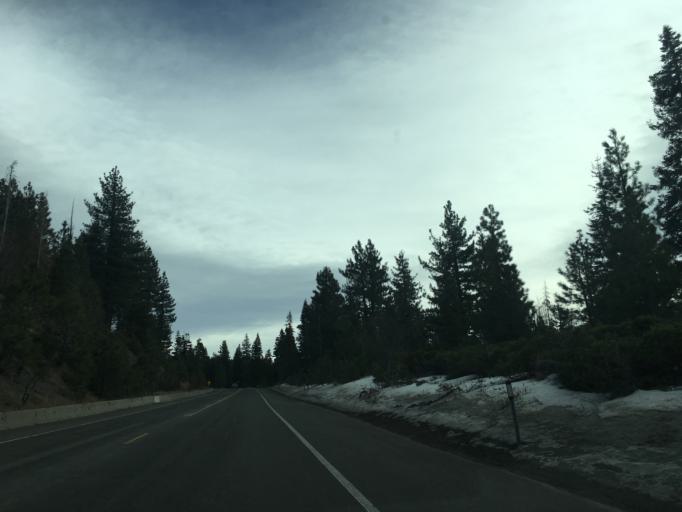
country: US
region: Nevada
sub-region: Washoe County
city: Incline Village
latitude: 39.2704
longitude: -119.9382
